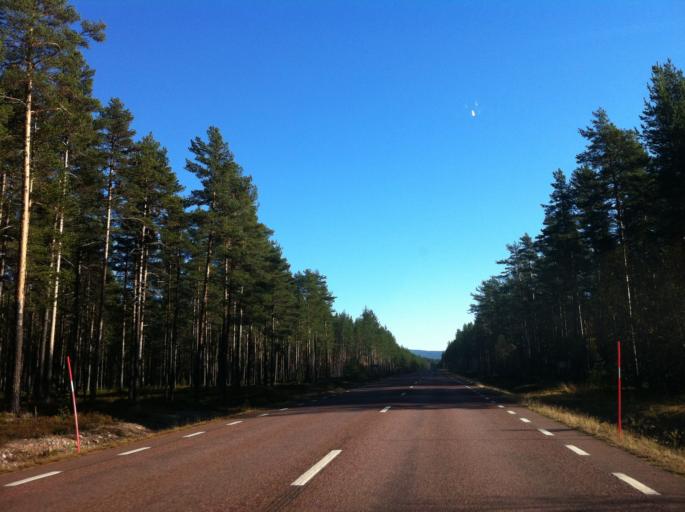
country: SE
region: Dalarna
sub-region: Alvdalens Kommun
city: AElvdalen
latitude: 61.2783
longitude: 13.9590
